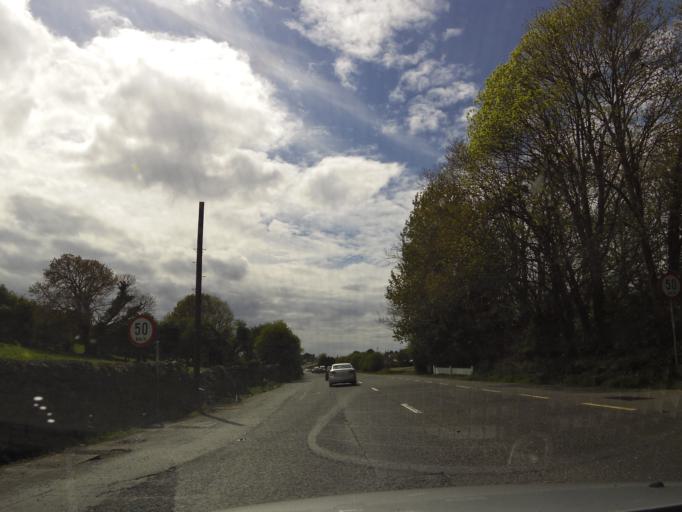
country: IE
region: Connaught
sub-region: County Galway
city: Gaillimh
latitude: 53.3035
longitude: -9.0033
